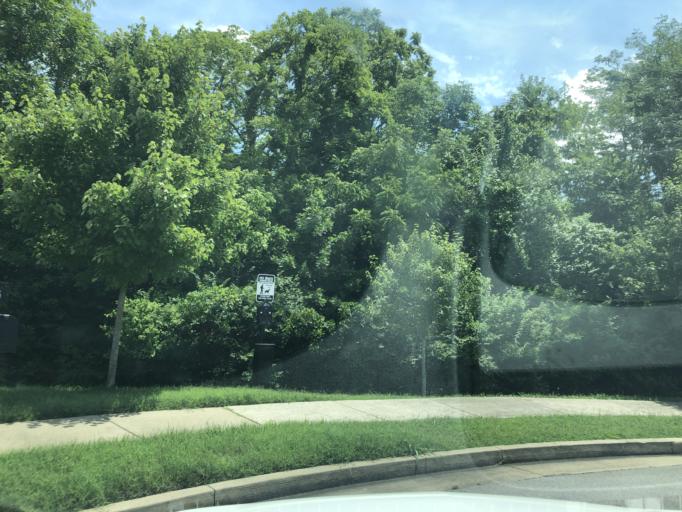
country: US
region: Tennessee
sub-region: Rutherford County
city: La Vergne
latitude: 36.0244
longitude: -86.6396
